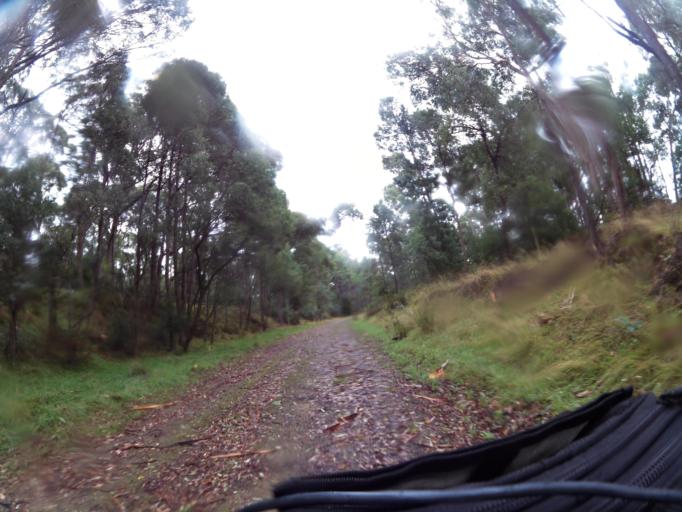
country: AU
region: New South Wales
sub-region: Greater Hume Shire
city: Holbrook
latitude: -36.1727
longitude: 147.4975
